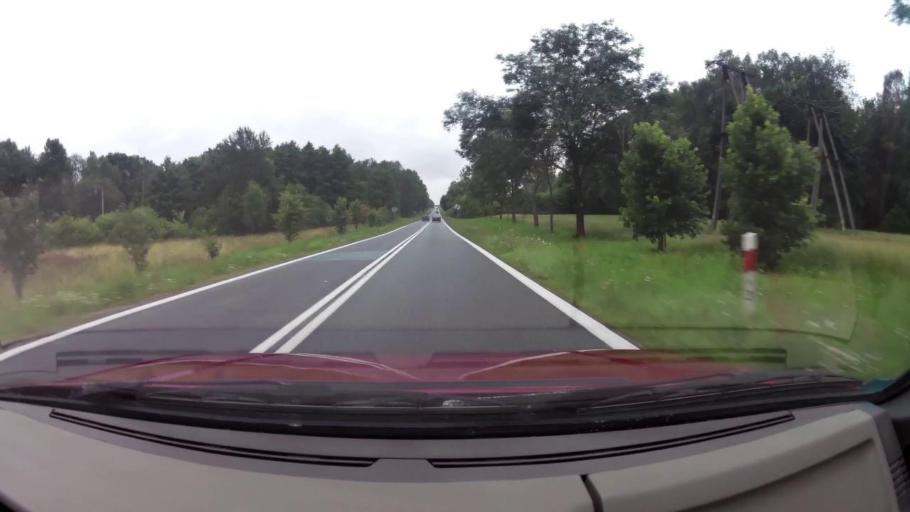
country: PL
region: West Pomeranian Voivodeship
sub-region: Powiat stargardzki
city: Chociwel
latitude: 53.4401
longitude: 15.3029
